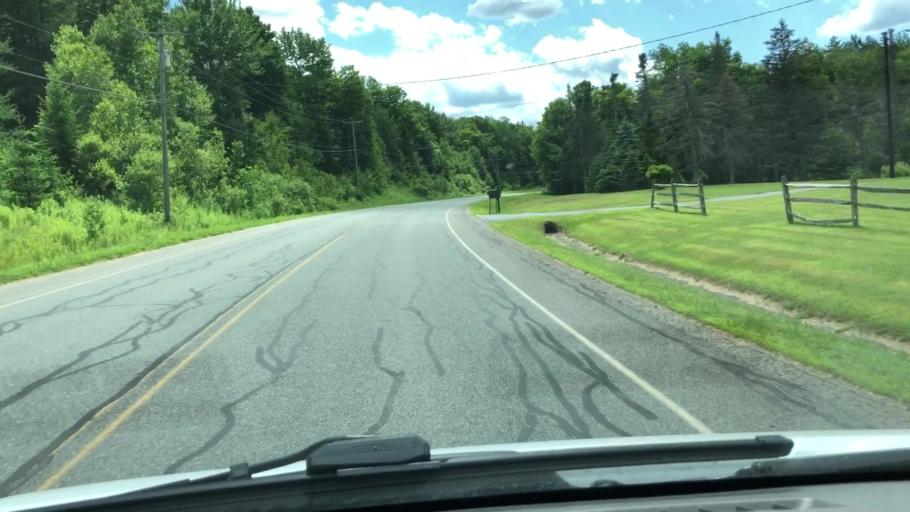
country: US
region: Massachusetts
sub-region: Berkshire County
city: Adams
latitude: 42.5658
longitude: -73.0407
